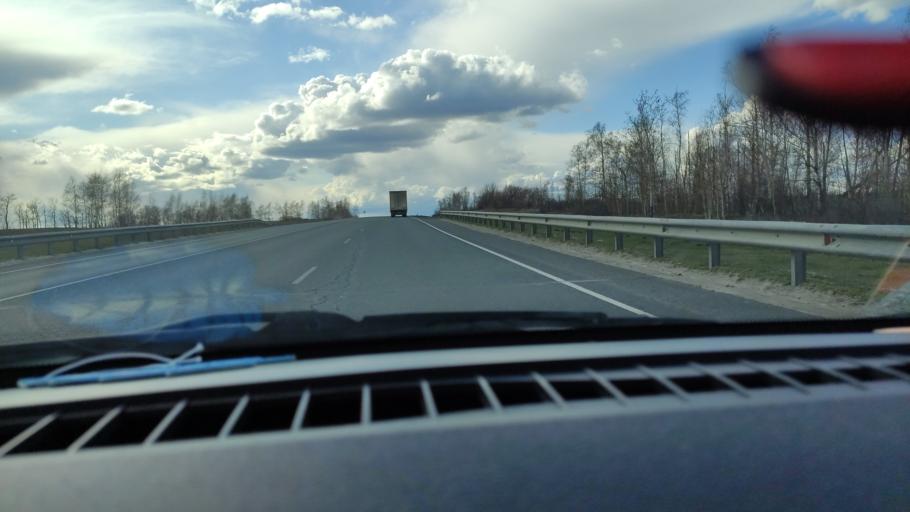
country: RU
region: Saratov
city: Shikhany
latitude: 52.1218
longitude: 47.2586
